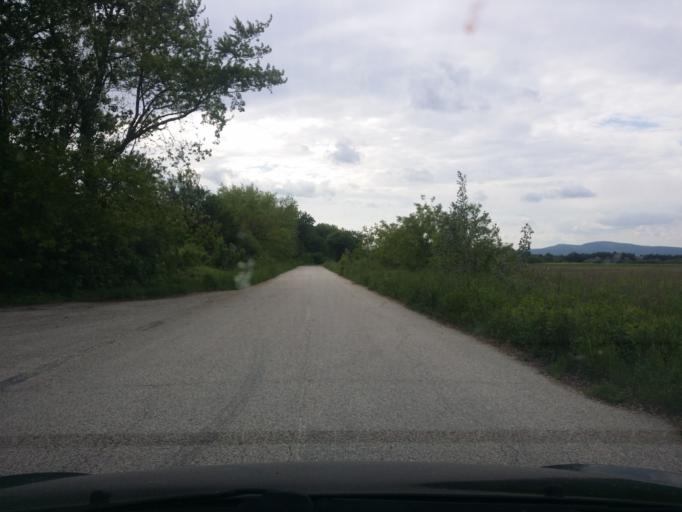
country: HU
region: Veszprem
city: Szentkiralyszabadja
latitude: 47.0867
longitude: 17.9738
